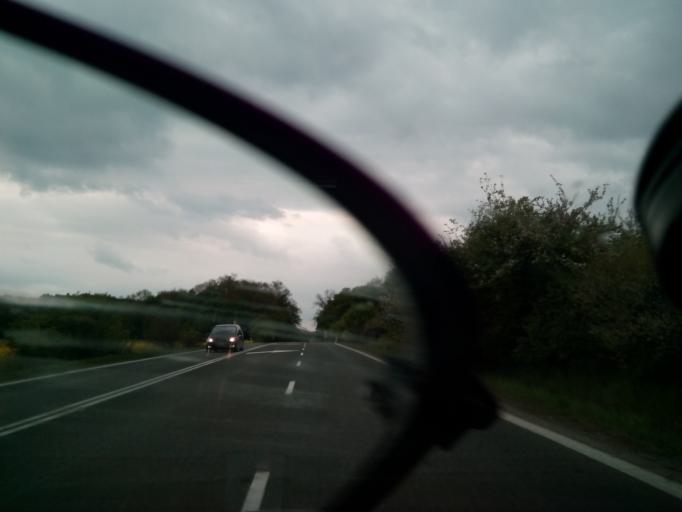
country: SK
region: Kosicky
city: Kosice
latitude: 48.7340
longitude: 21.3902
